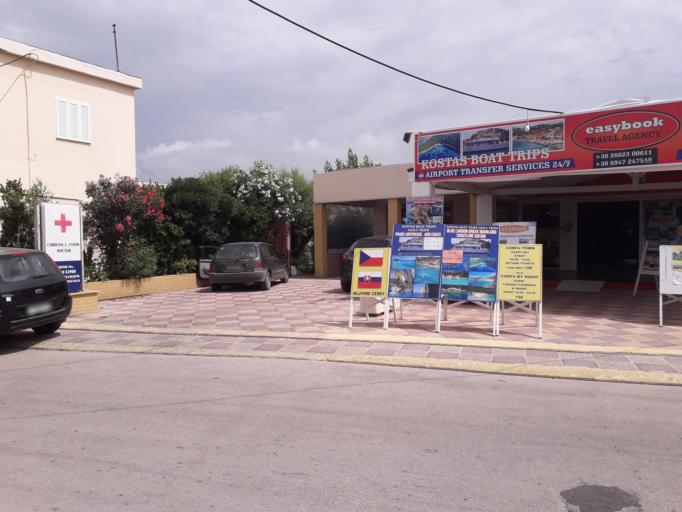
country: GR
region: Ionian Islands
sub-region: Nomos Kerkyras
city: Perivoli
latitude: 39.4260
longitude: 19.9456
